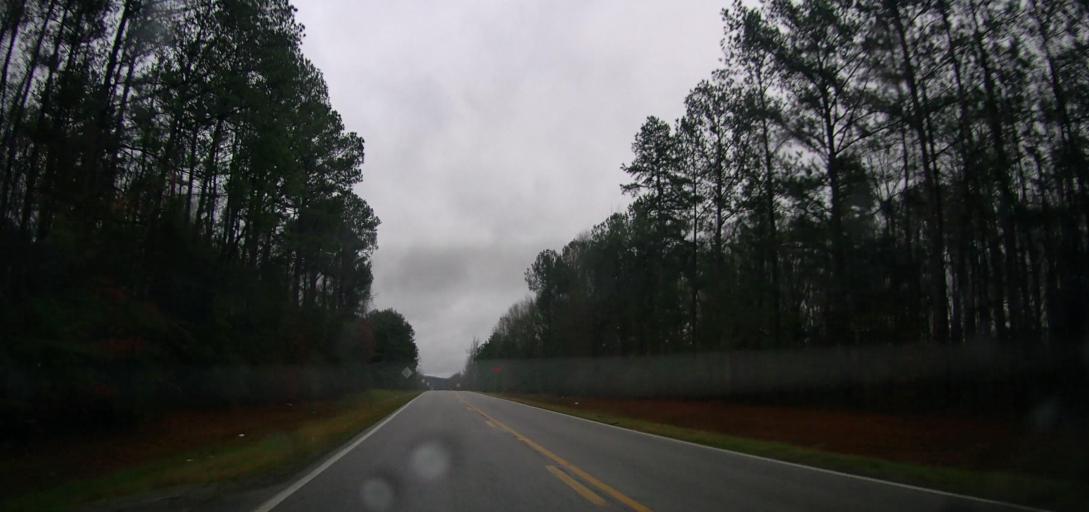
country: US
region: Alabama
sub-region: Bibb County
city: Centreville
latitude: 32.9276
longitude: -87.0483
